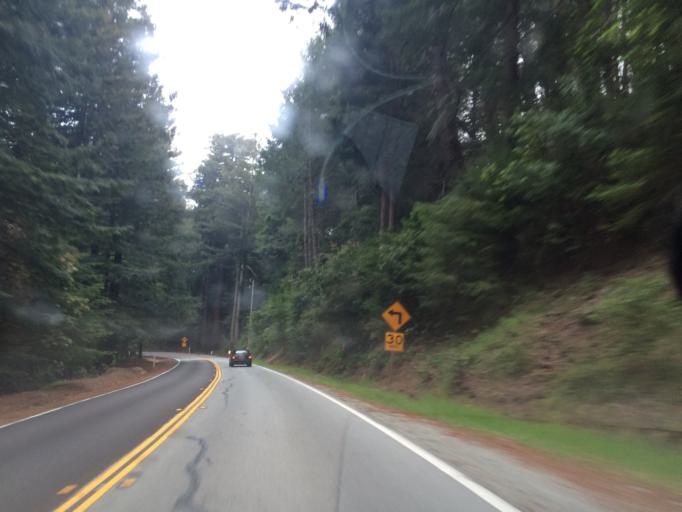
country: US
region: California
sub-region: Santa Cruz County
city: Boulder Creek
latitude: 37.2310
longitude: -122.1491
